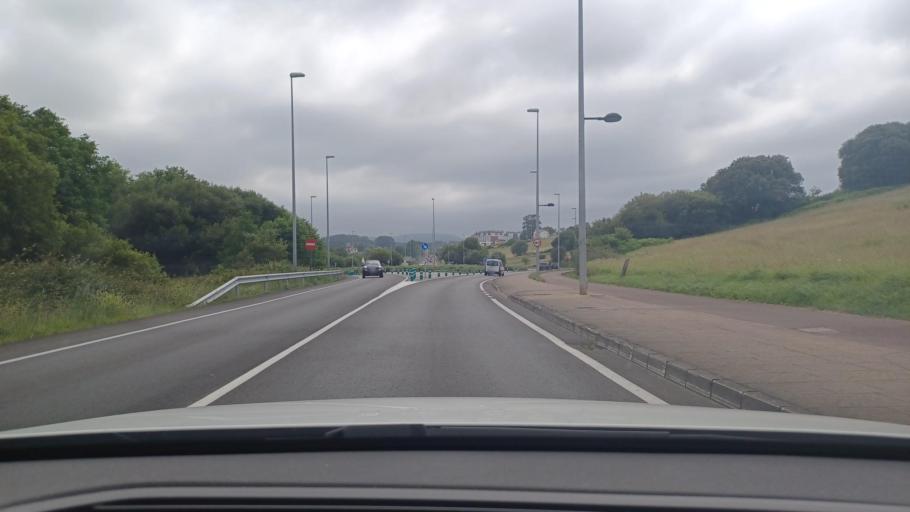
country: ES
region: Asturias
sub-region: Province of Asturias
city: Castrillon
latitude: 43.5670
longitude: -5.9649
